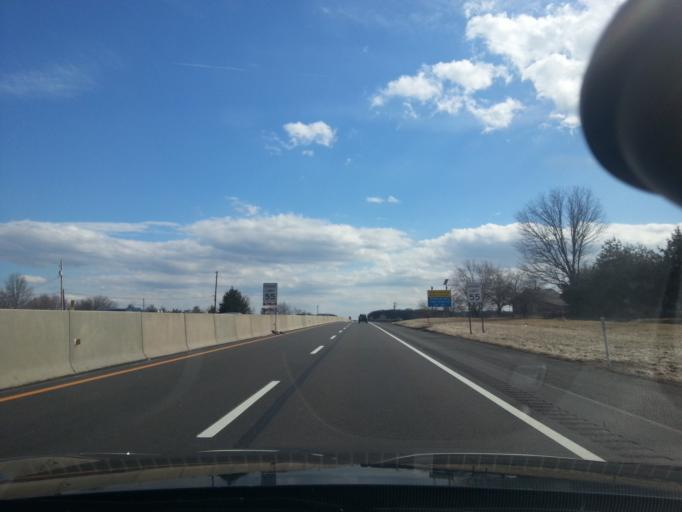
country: US
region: Pennsylvania
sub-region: Montgomery County
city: Harleysville
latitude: 40.2911
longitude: -75.3660
